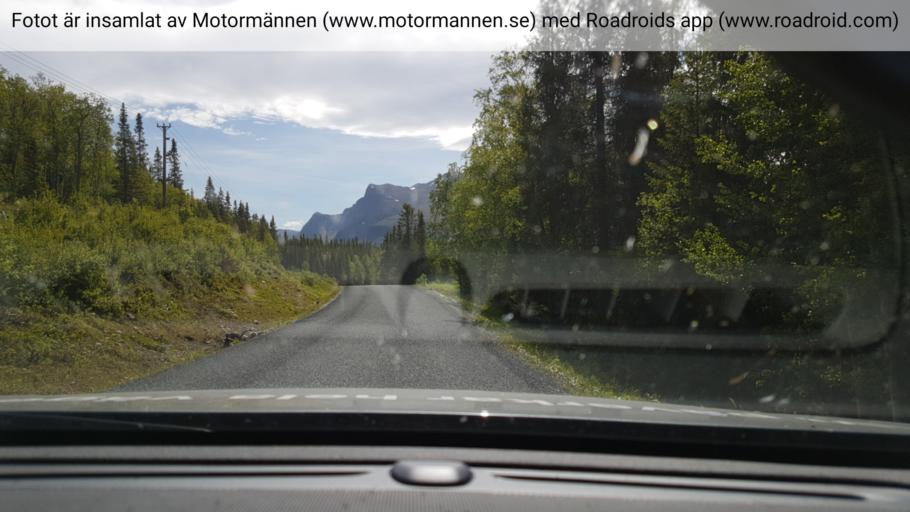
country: SE
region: Vaesterbotten
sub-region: Vilhelmina Kommun
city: Sjoberg
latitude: 65.2653
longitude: 15.3752
